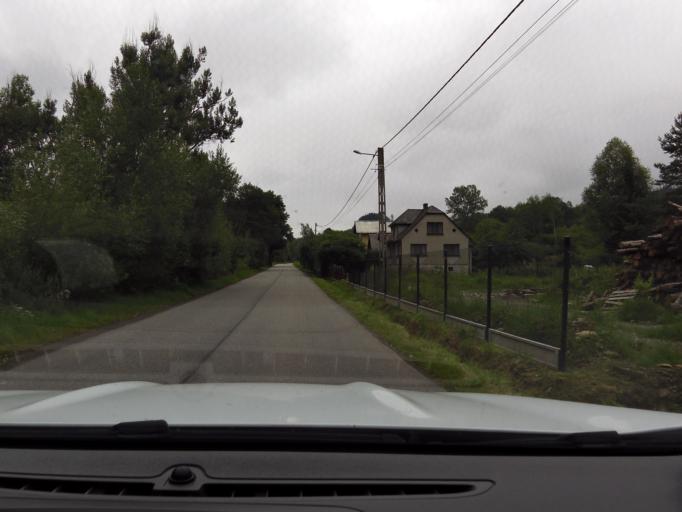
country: PL
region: Silesian Voivodeship
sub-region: Powiat zywiecki
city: Ujsoly
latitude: 49.4811
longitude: 19.1510
